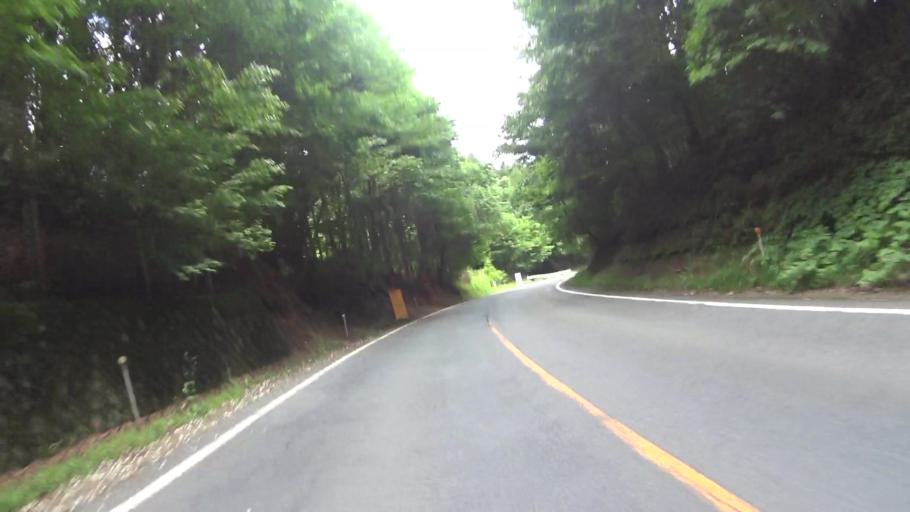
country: JP
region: Kumamoto
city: Aso
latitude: 33.0805
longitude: 131.1968
